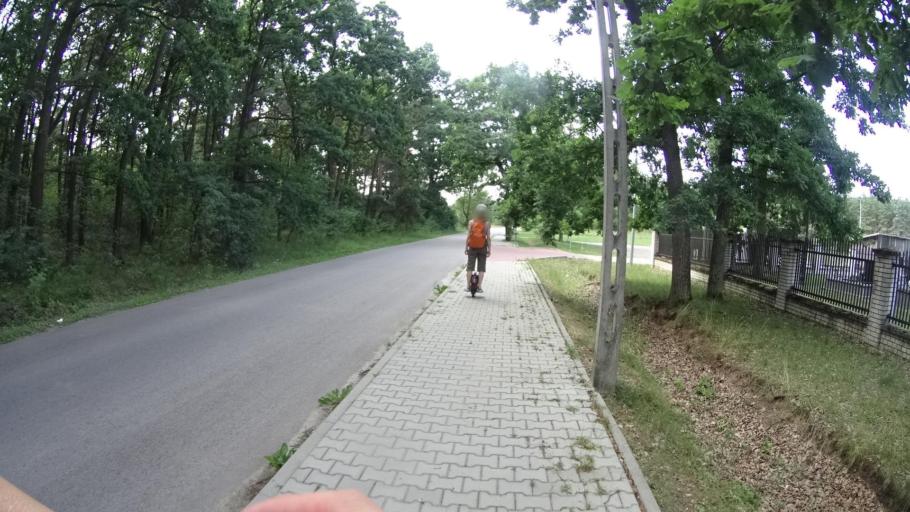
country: PL
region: Masovian Voivodeship
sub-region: Powiat bialobrzeski
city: Bialobrzegi
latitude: 51.6445
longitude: 20.9666
